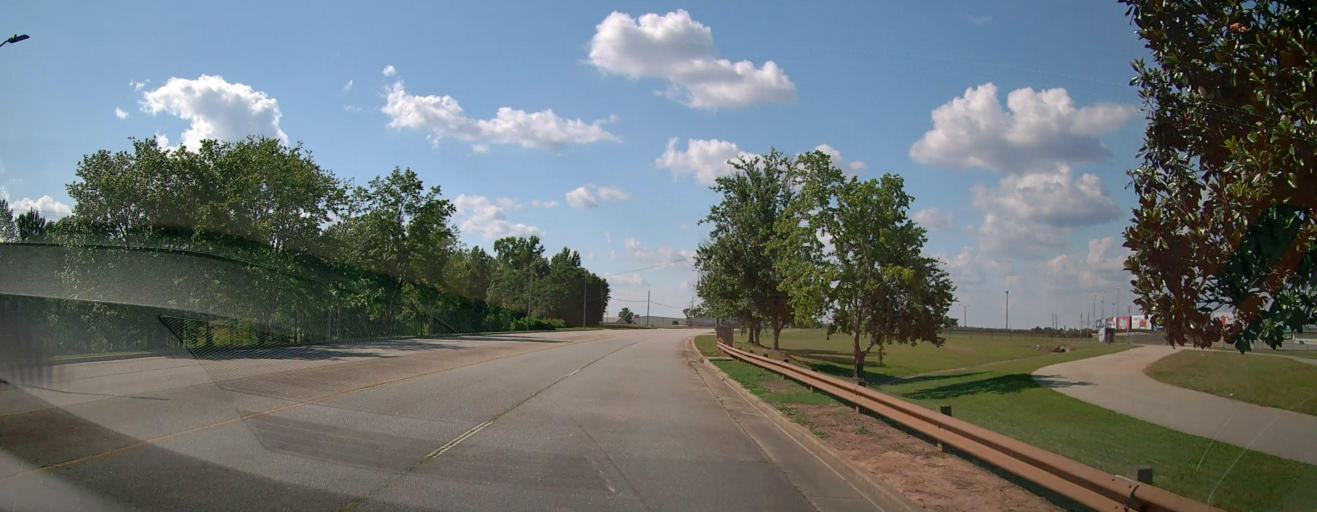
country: US
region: Georgia
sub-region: Henry County
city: Hampton
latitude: 33.3807
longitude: -84.3242
